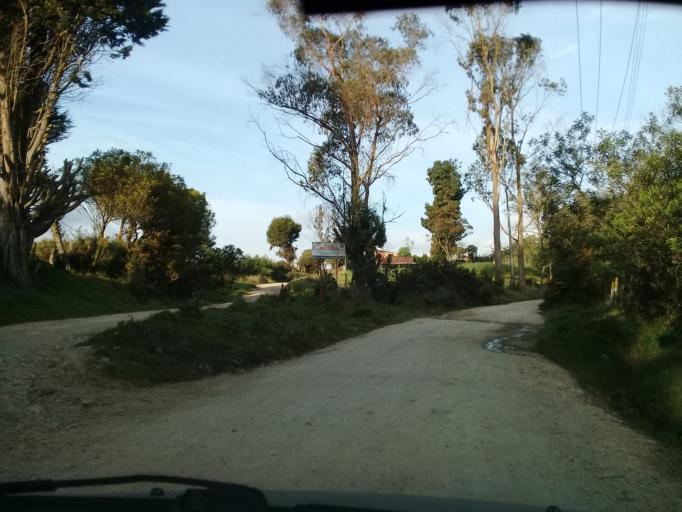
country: CO
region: Cundinamarca
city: Sibate
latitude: 4.4496
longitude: -74.2745
